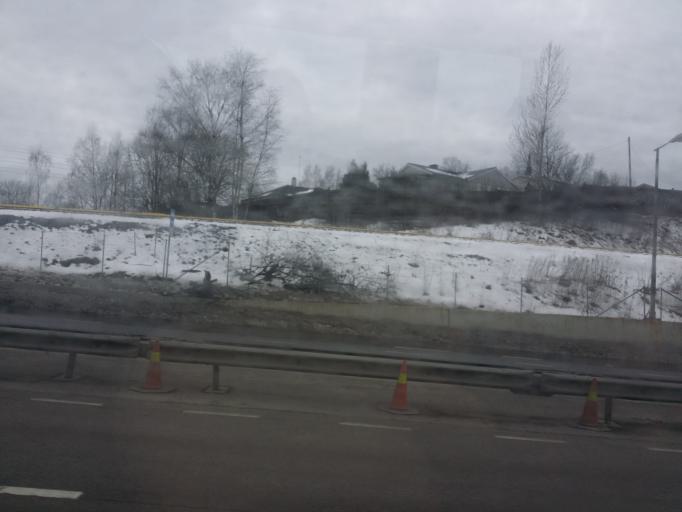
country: NO
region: Oslo
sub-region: Oslo
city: Oslo
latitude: 59.9040
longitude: 10.8207
